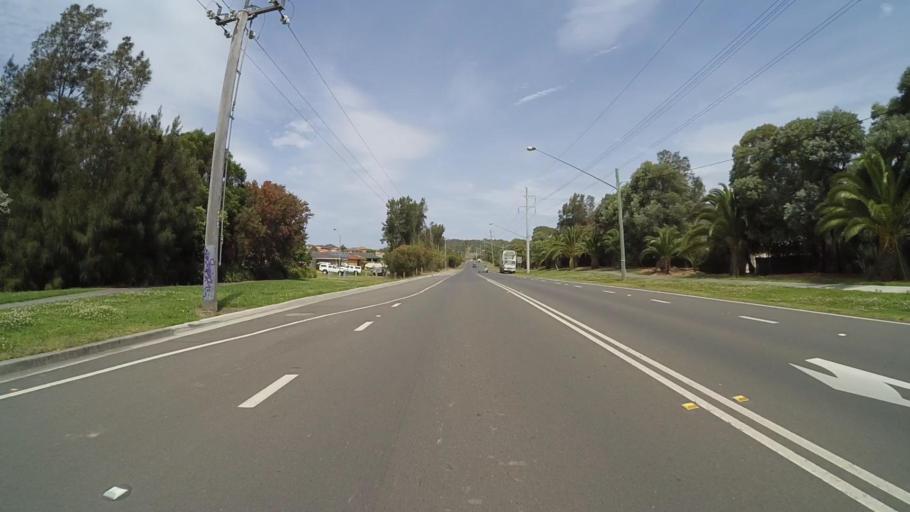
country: AU
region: New South Wales
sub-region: Shellharbour
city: Albion Park Rail
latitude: -34.5859
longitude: 150.7795
